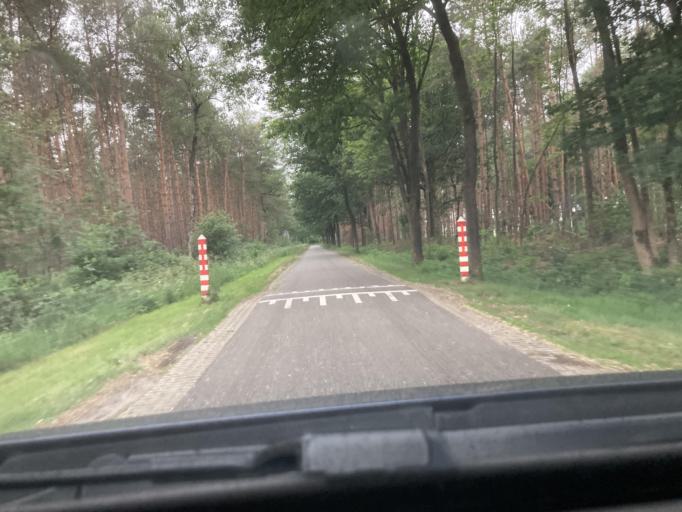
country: NL
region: North Brabant
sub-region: Gemeente Hilvarenbeek
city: Hilvarenbeek
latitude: 51.4373
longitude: 5.1306
